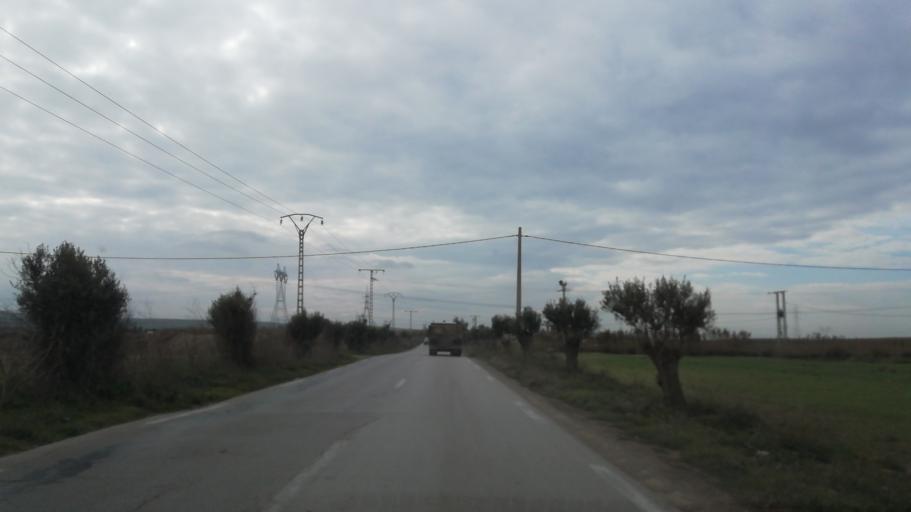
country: DZ
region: Oran
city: Ain el Bya
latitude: 35.7763
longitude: -0.3458
